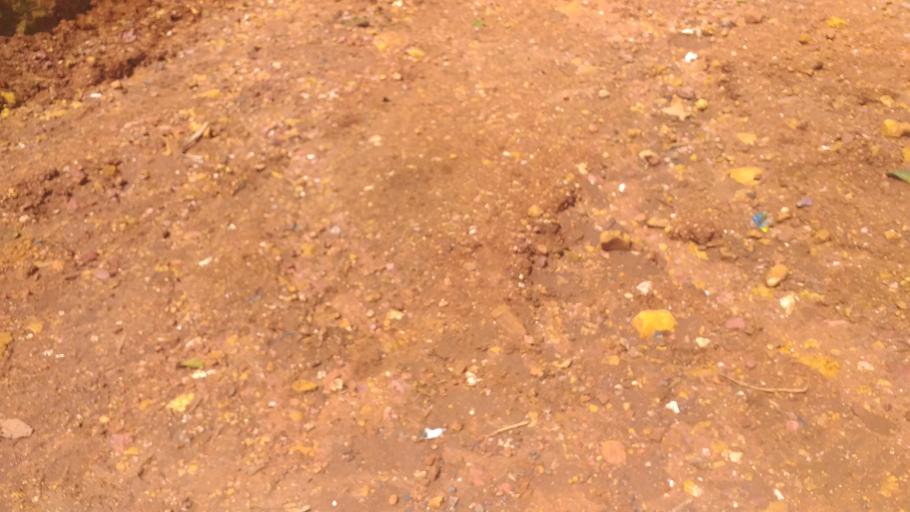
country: ET
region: Southern Nations, Nationalities, and People's Region
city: Bako
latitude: 5.9821
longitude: 36.5289
